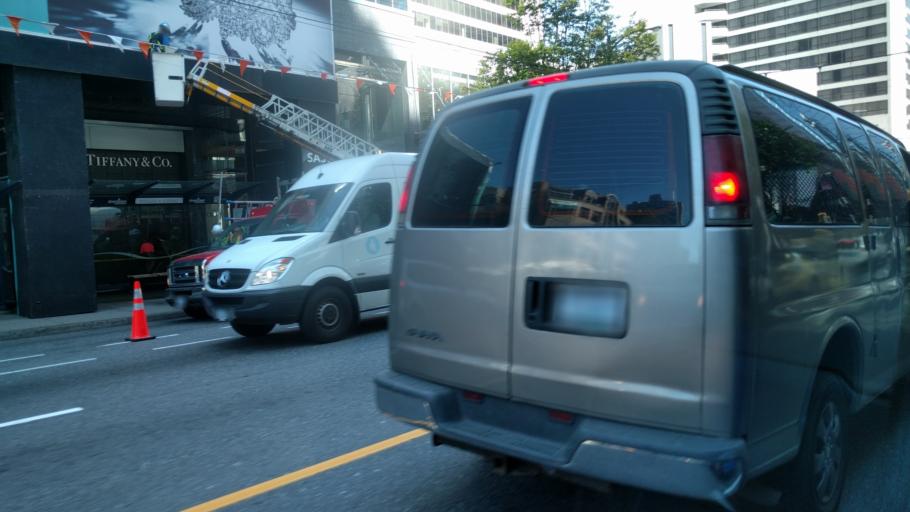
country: CA
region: British Columbia
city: West End
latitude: 49.2841
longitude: -123.1216
